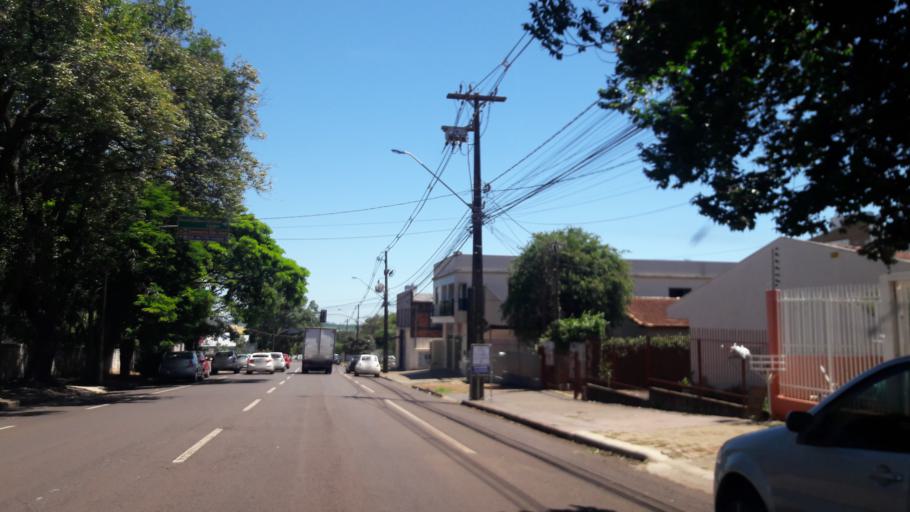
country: BR
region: Parana
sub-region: Cascavel
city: Cascavel
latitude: -24.9521
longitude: -53.4752
